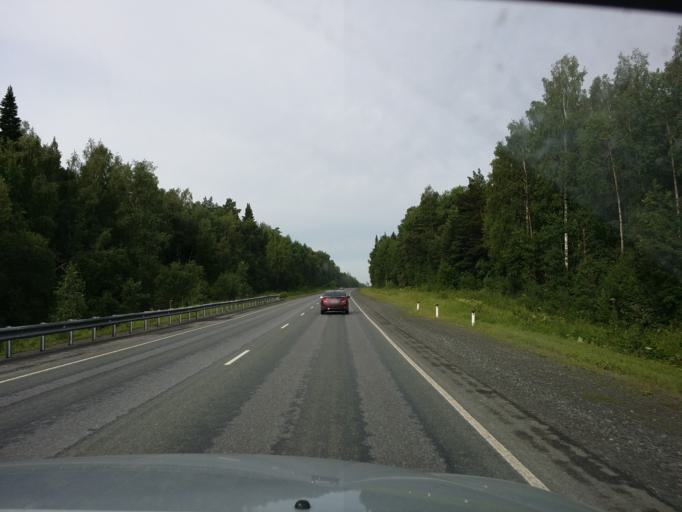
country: RU
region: Tjumen
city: Abalak
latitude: 58.4774
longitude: 68.6127
